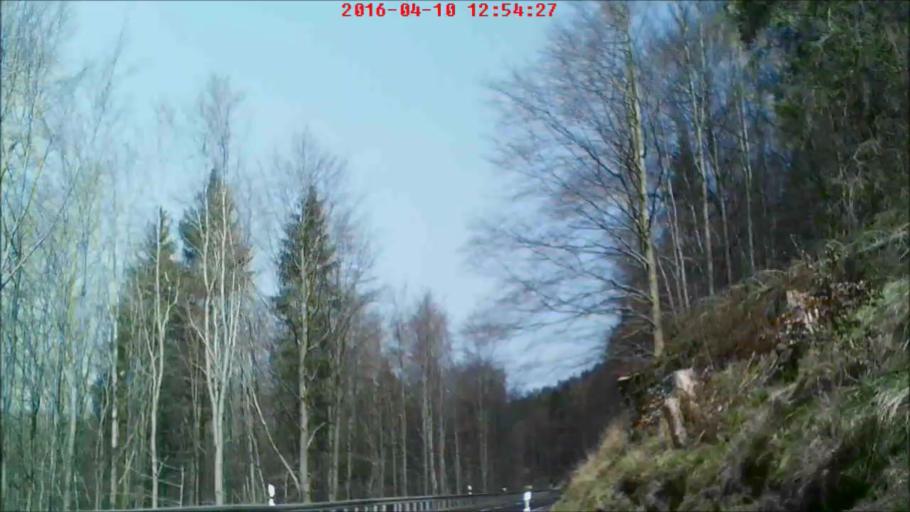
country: DE
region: Thuringia
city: Pappenheim
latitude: 50.8178
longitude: 10.5183
